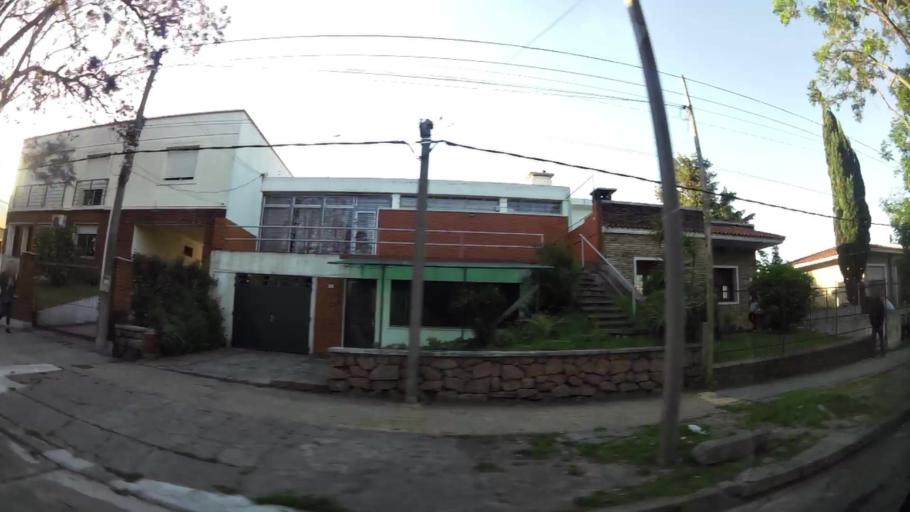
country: UY
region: Montevideo
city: Montevideo
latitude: -34.8418
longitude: -56.2045
